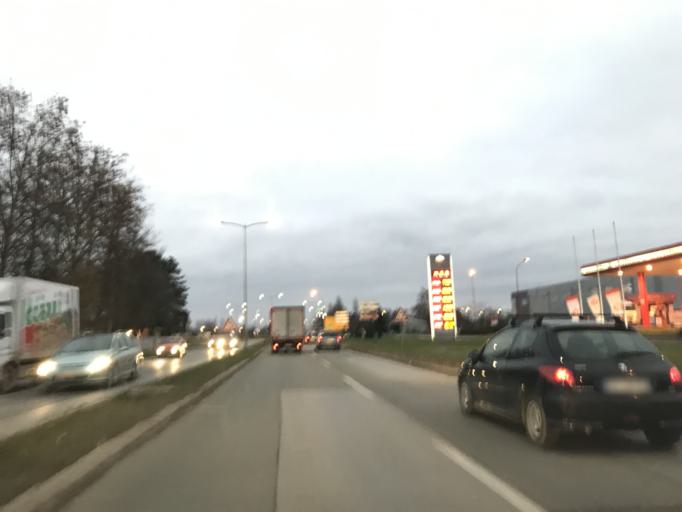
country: RS
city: Veternik
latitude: 45.2764
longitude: 19.7986
